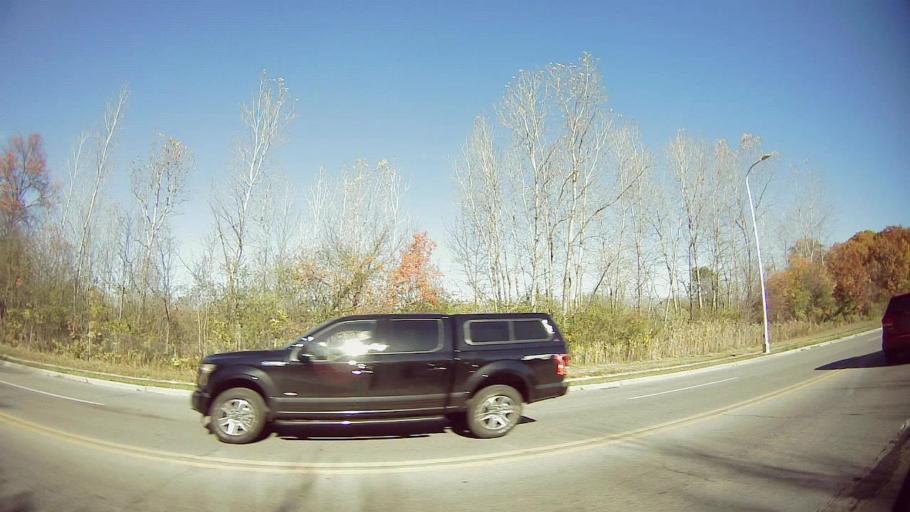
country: US
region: Michigan
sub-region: Wayne County
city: Dearborn Heights
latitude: 42.3574
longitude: -83.2577
